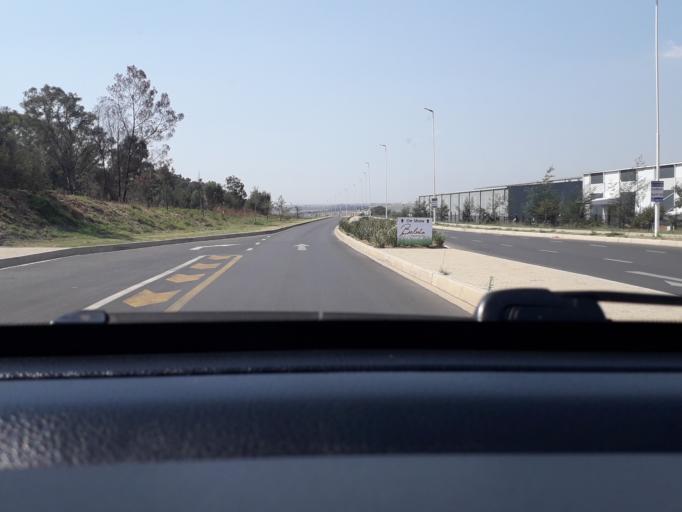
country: ZA
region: Gauteng
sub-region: City of Johannesburg Metropolitan Municipality
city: Modderfontein
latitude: -26.0992
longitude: 28.1387
